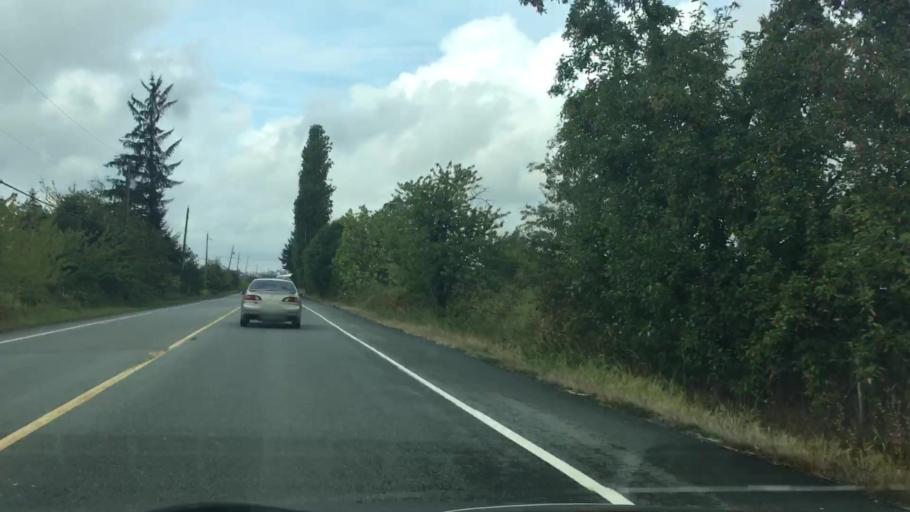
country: CA
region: British Columbia
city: Langley
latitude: 49.1043
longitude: -122.6112
